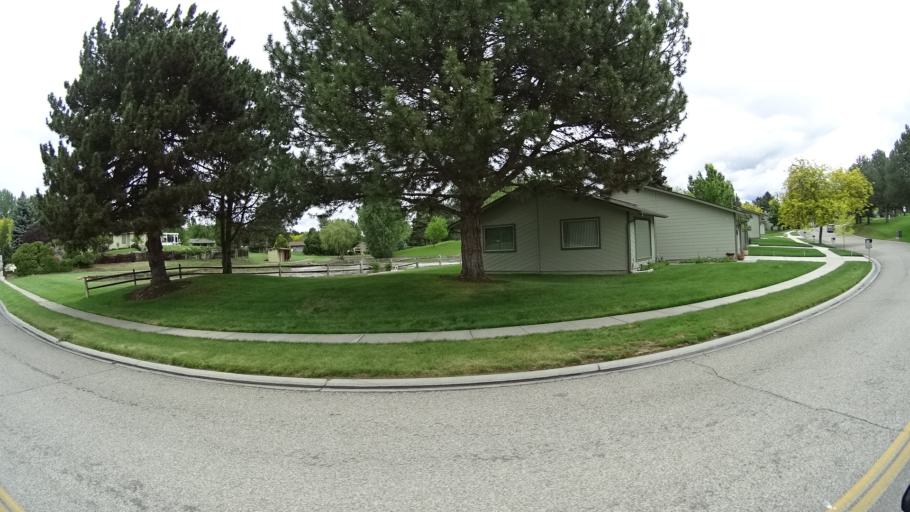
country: US
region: Idaho
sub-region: Ada County
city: Eagle
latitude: 43.7016
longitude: -116.3420
